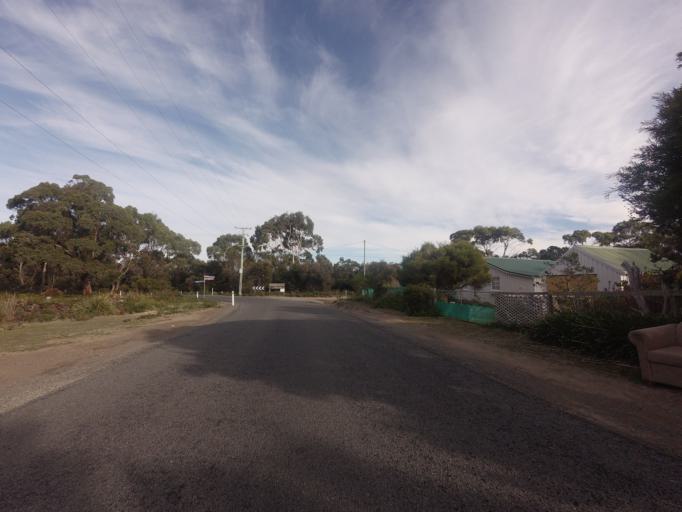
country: AU
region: Tasmania
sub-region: Sorell
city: Sorell
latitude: -42.9696
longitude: 147.8318
